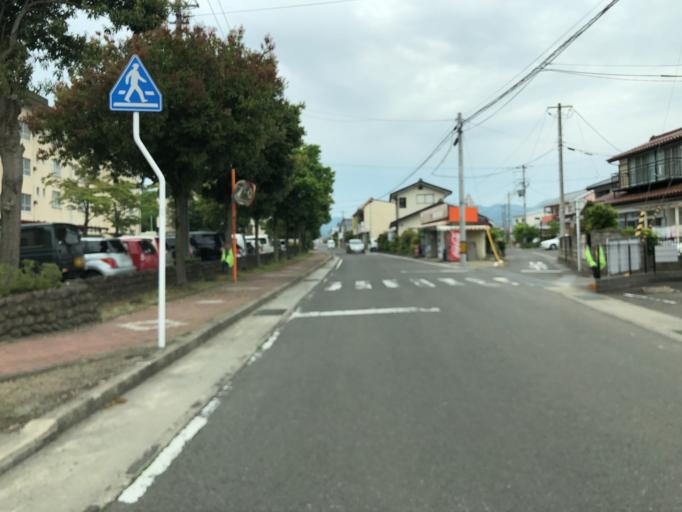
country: JP
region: Fukushima
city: Fukushima-shi
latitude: 37.7824
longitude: 140.4302
